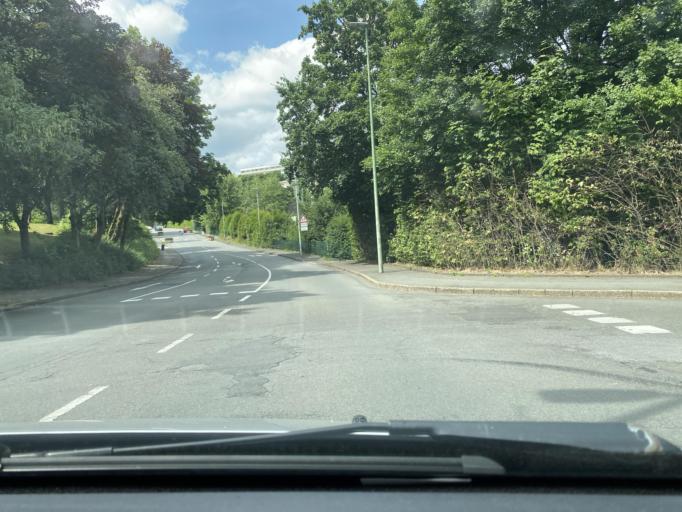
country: DE
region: North Rhine-Westphalia
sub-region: Regierungsbezirk Arnsberg
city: Luedenscheid
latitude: 51.2313
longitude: 7.6253
